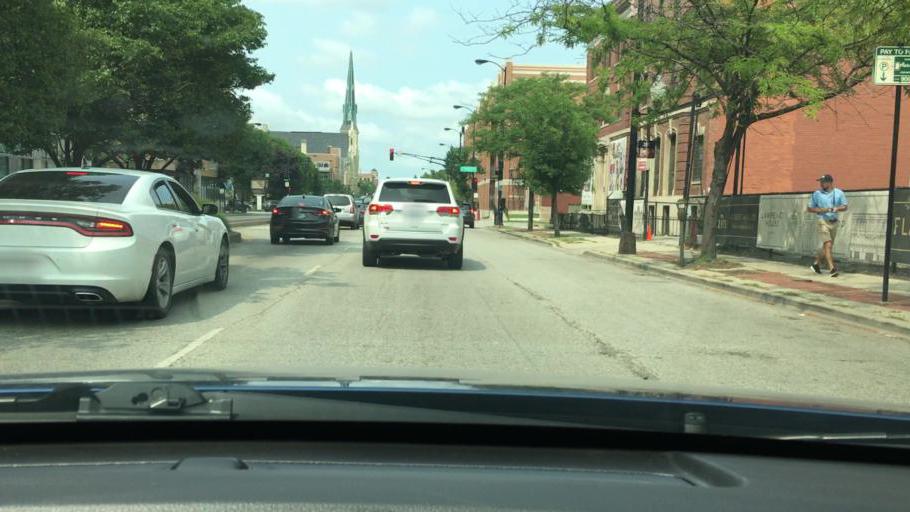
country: US
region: Illinois
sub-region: Cook County
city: Chicago
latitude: 41.8795
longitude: -87.6667
